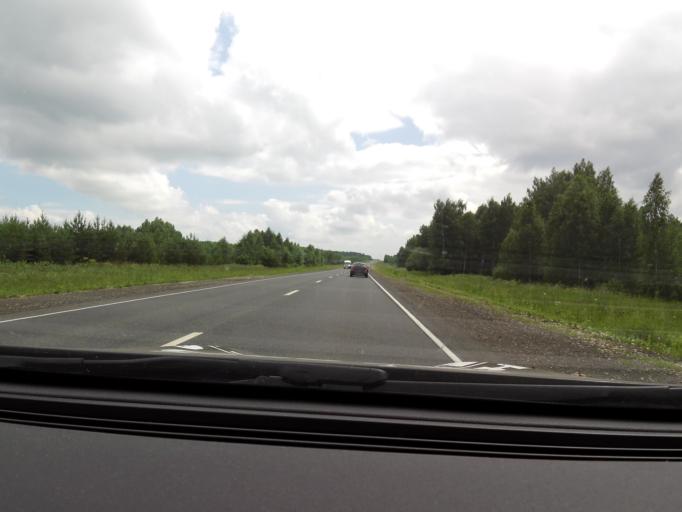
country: RU
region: Perm
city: Orda
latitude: 57.2363
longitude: 57.0620
